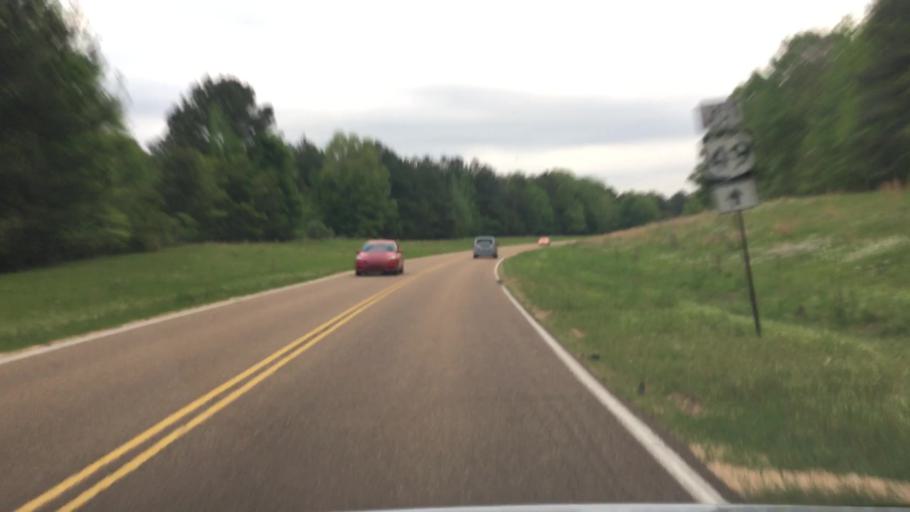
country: US
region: Mississippi
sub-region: Hinds County
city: Clinton
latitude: 32.3791
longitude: -90.2683
